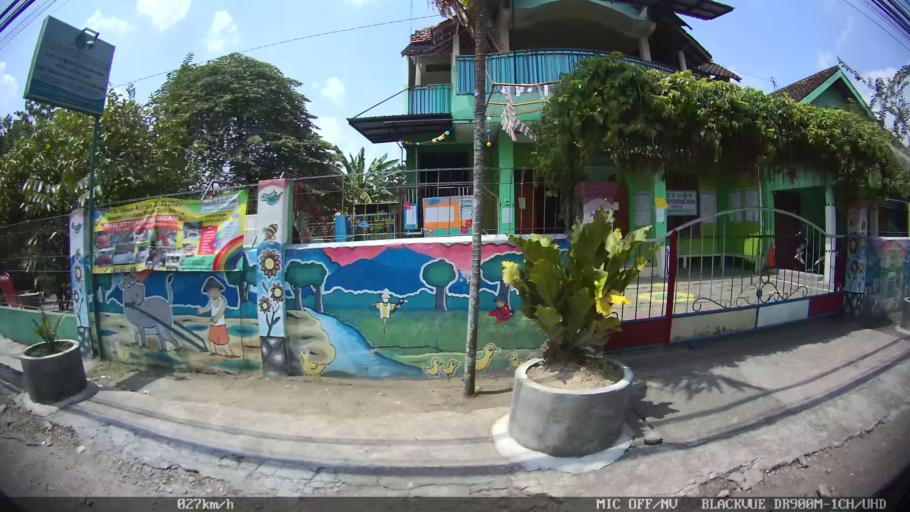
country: ID
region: Daerah Istimewa Yogyakarta
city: Yogyakarta
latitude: -7.8236
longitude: 110.4078
